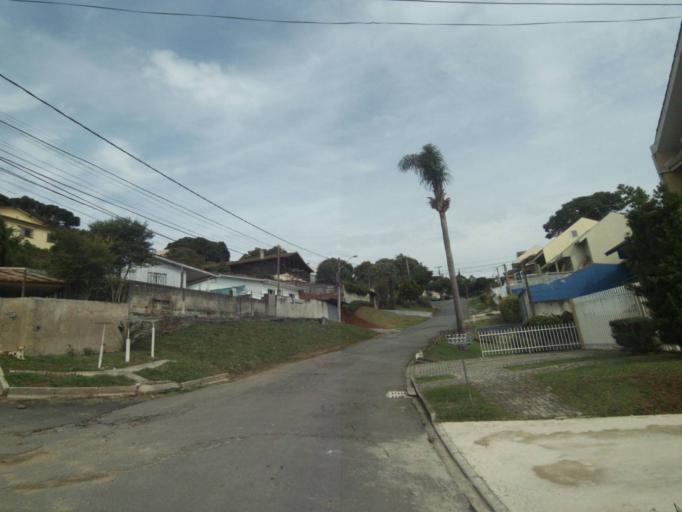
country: BR
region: Parana
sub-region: Curitiba
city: Curitiba
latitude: -25.4119
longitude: -49.2984
